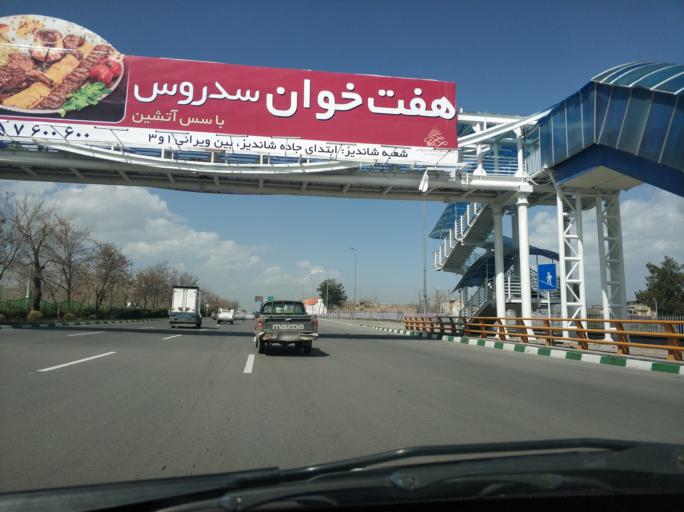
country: IR
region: Razavi Khorasan
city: Torqabeh
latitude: 36.3413
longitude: 59.4582
